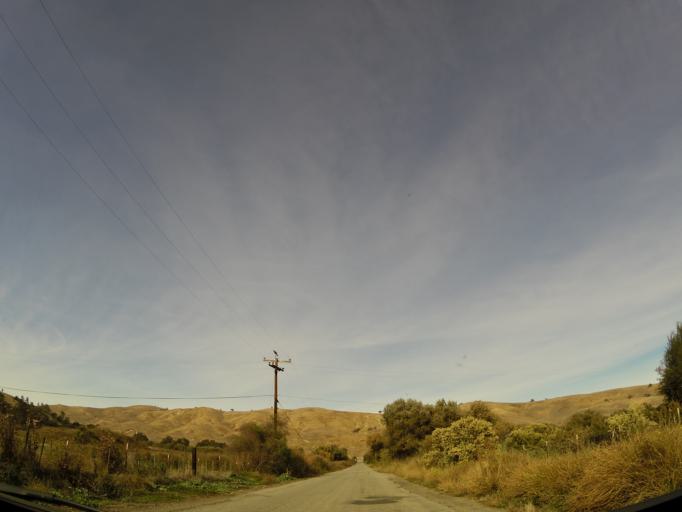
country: US
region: California
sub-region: San Benito County
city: Ridgemark
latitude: 36.7017
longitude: -121.3295
